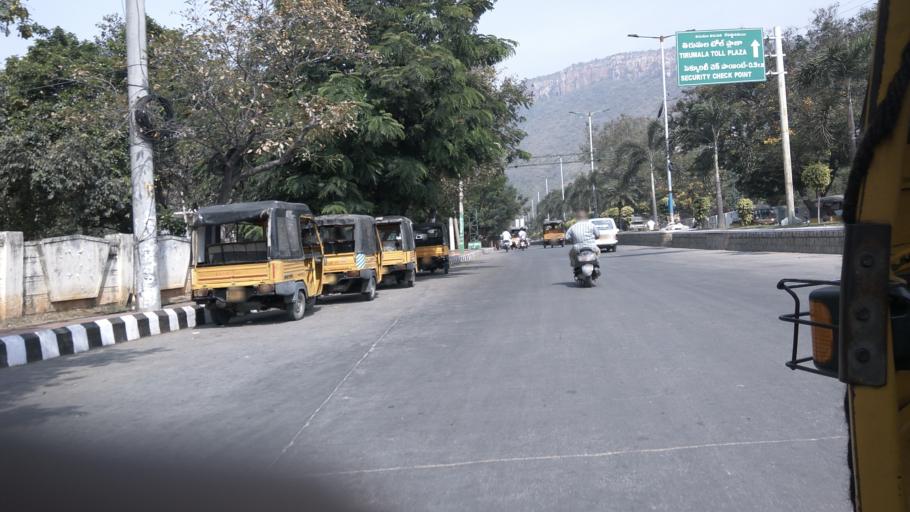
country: IN
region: Andhra Pradesh
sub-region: Chittoor
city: Tirupati
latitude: 13.6428
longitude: 79.4088
